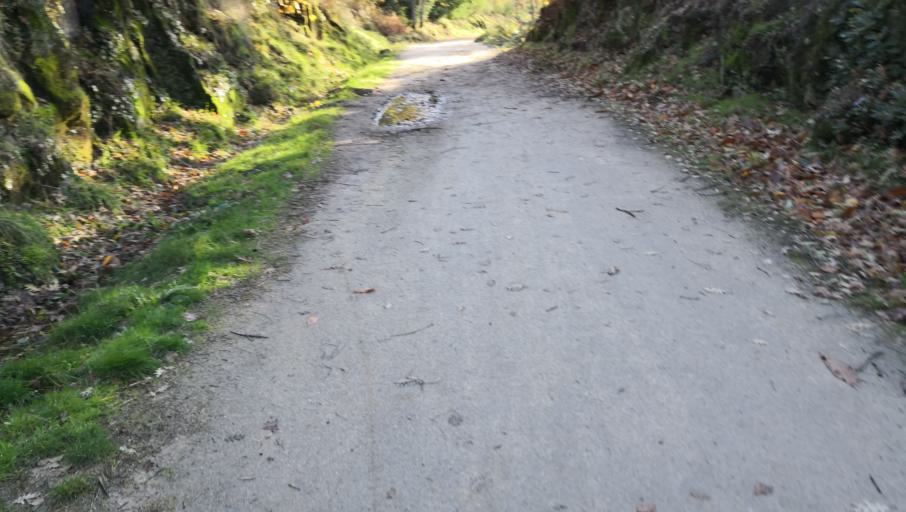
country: PT
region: Vila Real
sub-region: Vila Real
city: Vila Real
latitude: 41.3243
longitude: -7.7106
